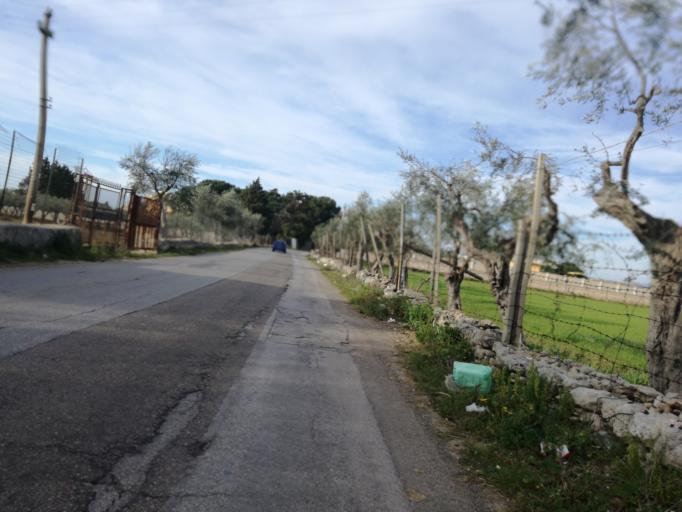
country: IT
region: Apulia
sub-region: Provincia di Bari
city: Capurso
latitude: 41.0535
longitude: 16.9216
